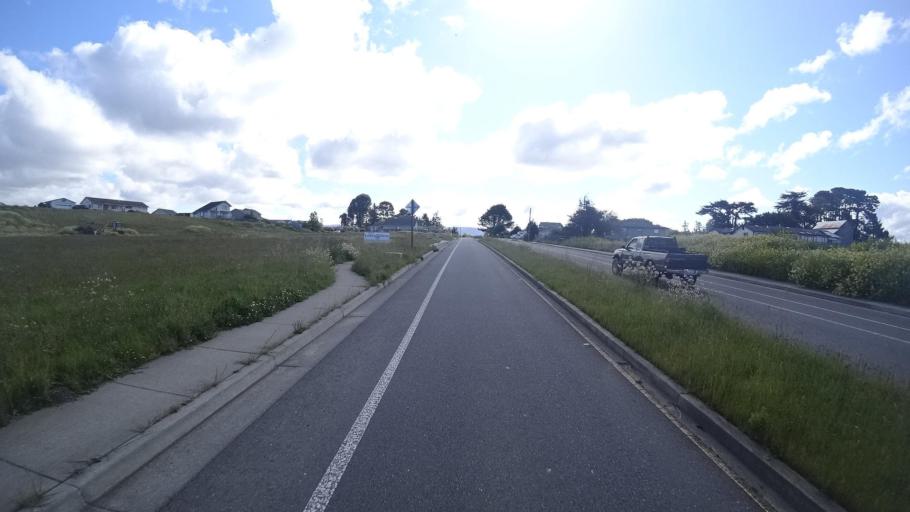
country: US
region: California
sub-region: Humboldt County
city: McKinleyville
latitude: 40.9343
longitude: -124.1111
